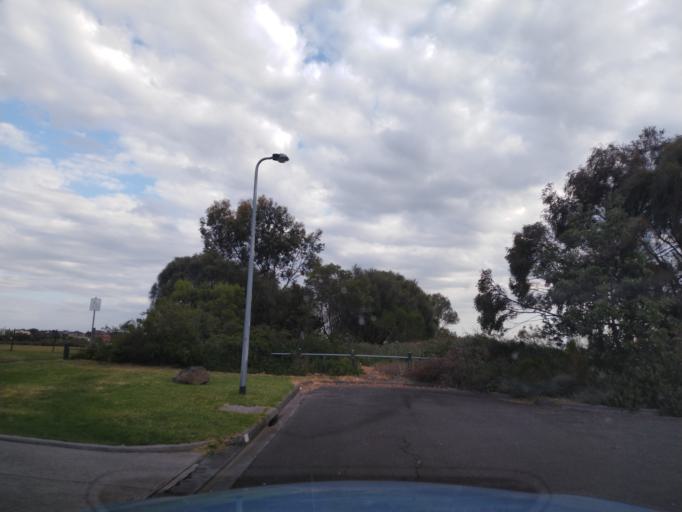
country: AU
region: Victoria
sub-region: Hobsons Bay
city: Williamstown North
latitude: -37.8583
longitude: 144.8741
